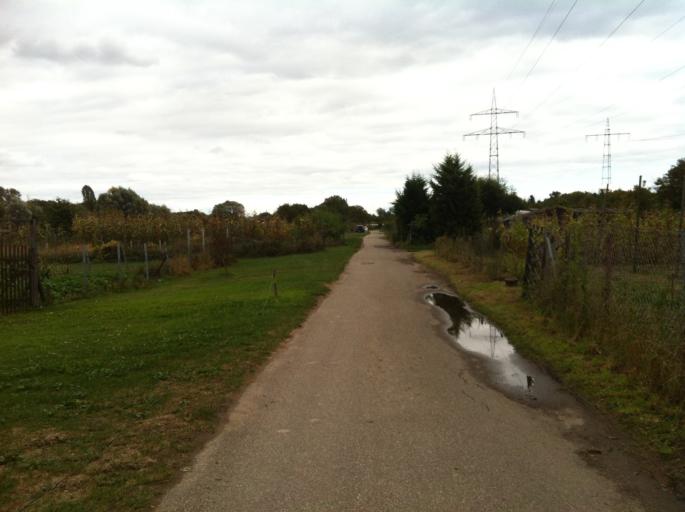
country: DE
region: Rheinland-Pfalz
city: Budenheim
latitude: 50.0307
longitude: 8.1921
